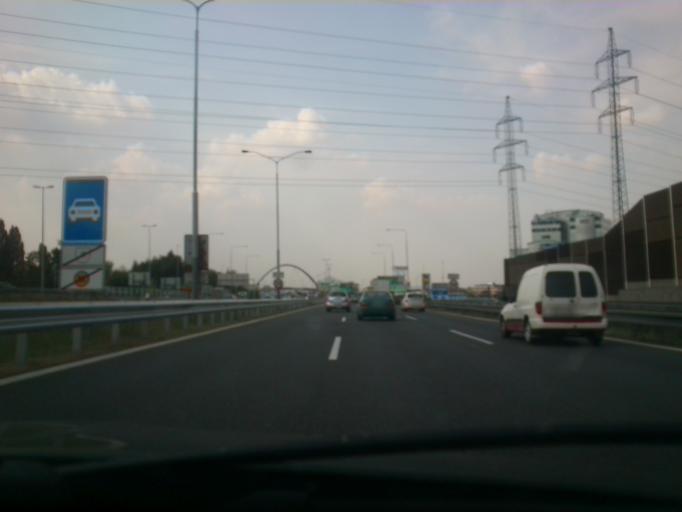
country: CZ
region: Central Bohemia
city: Vestec
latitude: 50.0329
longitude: 14.4926
